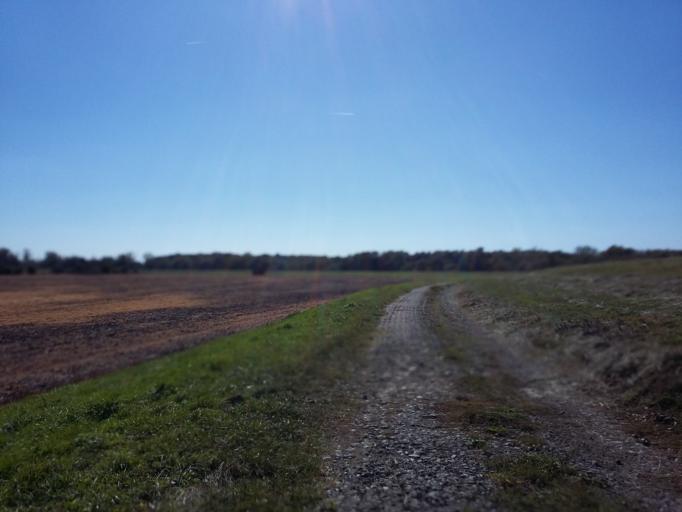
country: AT
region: Lower Austria
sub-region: Politischer Bezirk Ganserndorf
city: Marchegg
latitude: 48.3058
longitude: 16.9248
